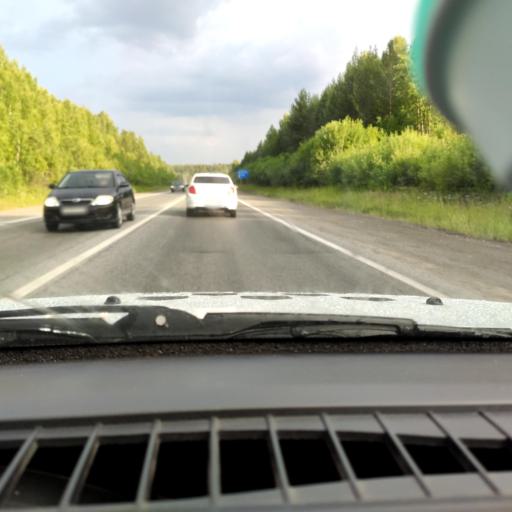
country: RU
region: Sverdlovsk
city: Talitsa
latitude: 56.8542
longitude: 60.0569
